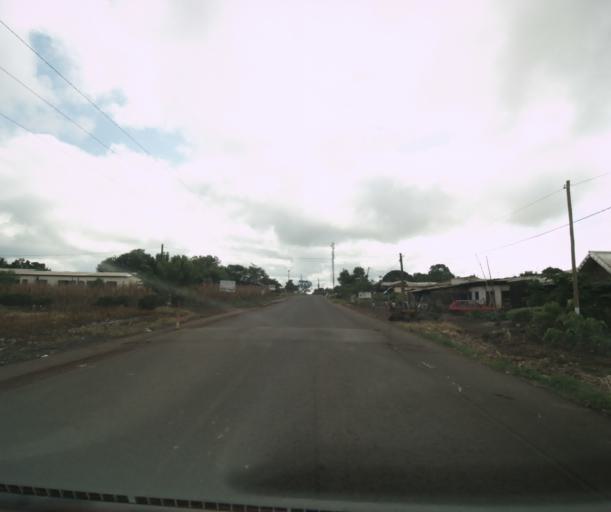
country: CM
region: West
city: Foumbot
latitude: 5.5046
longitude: 10.6219
